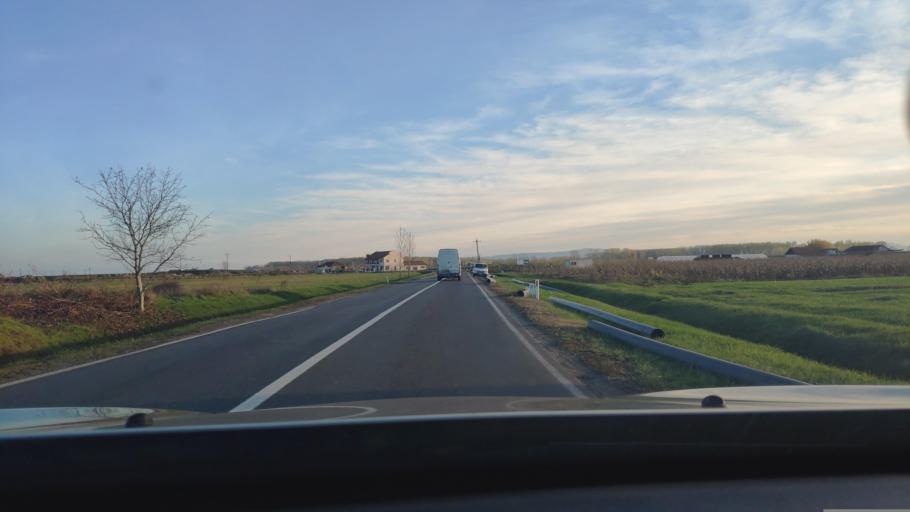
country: RO
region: Satu Mare
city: Culciu Mic
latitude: 47.7872
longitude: 23.0545
